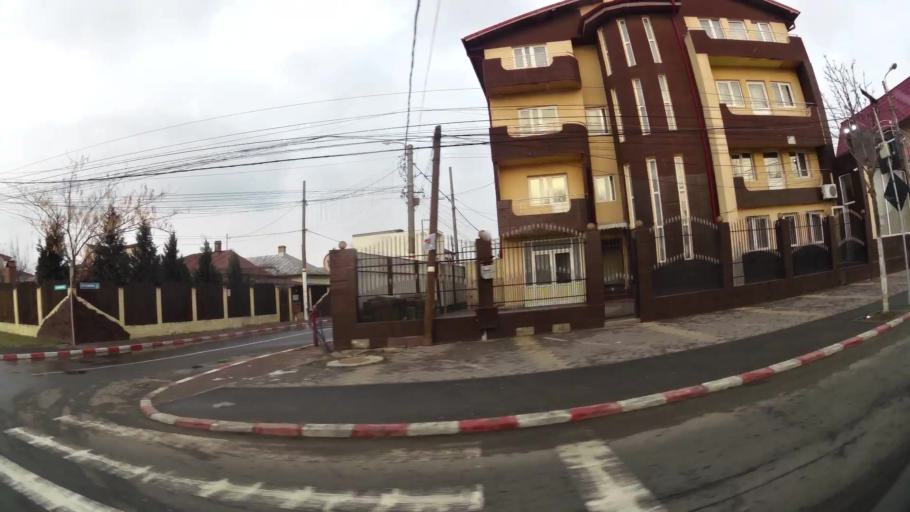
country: RO
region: Ilfov
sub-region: Voluntari City
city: Voluntari
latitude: 44.4869
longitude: 26.1749
